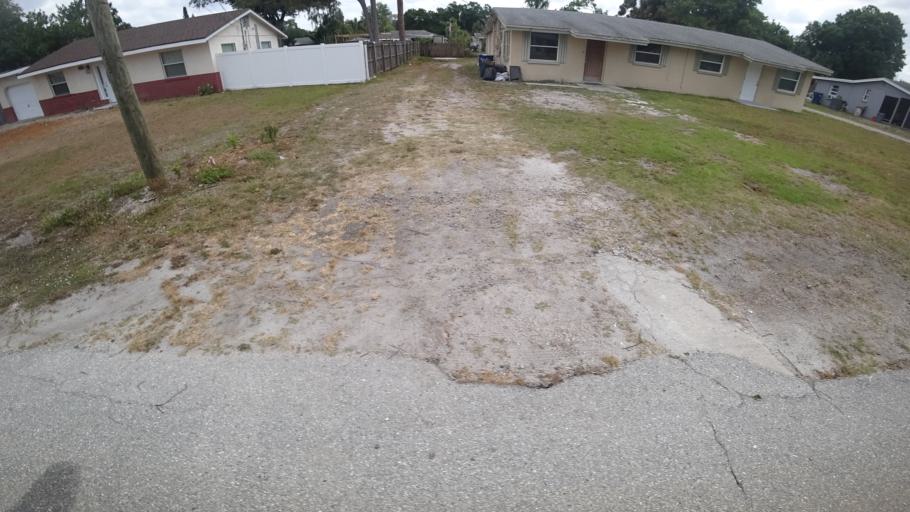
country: US
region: Florida
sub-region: Manatee County
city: Bayshore Gardens
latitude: 27.4430
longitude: -82.5840
